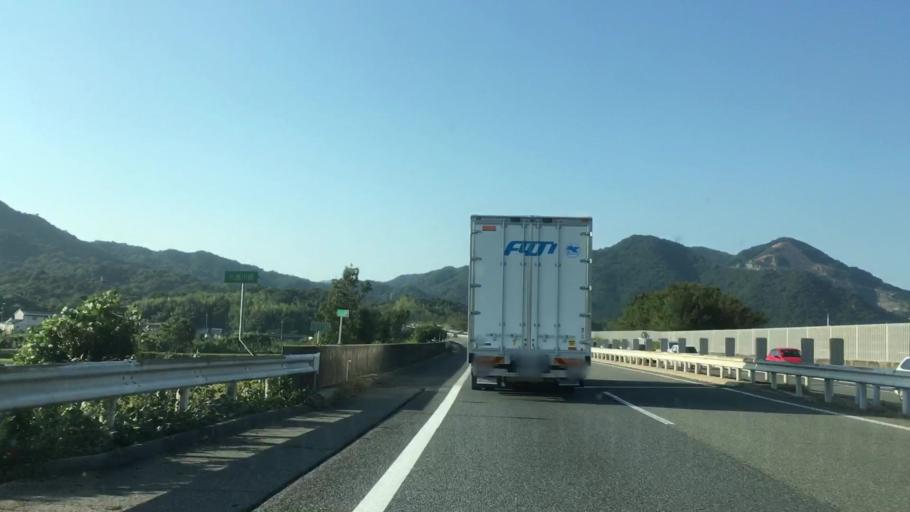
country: JP
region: Yamaguchi
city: Hofu
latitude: 34.0695
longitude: 131.4986
